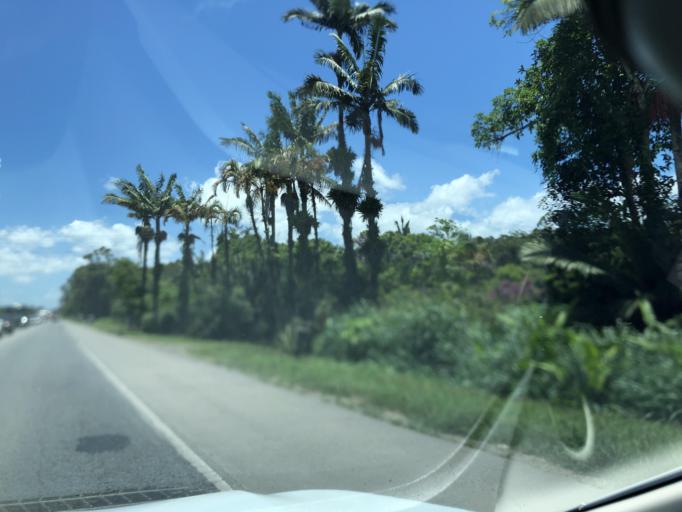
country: BR
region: Santa Catarina
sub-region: Joinville
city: Joinville
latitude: -26.4144
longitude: -48.7631
